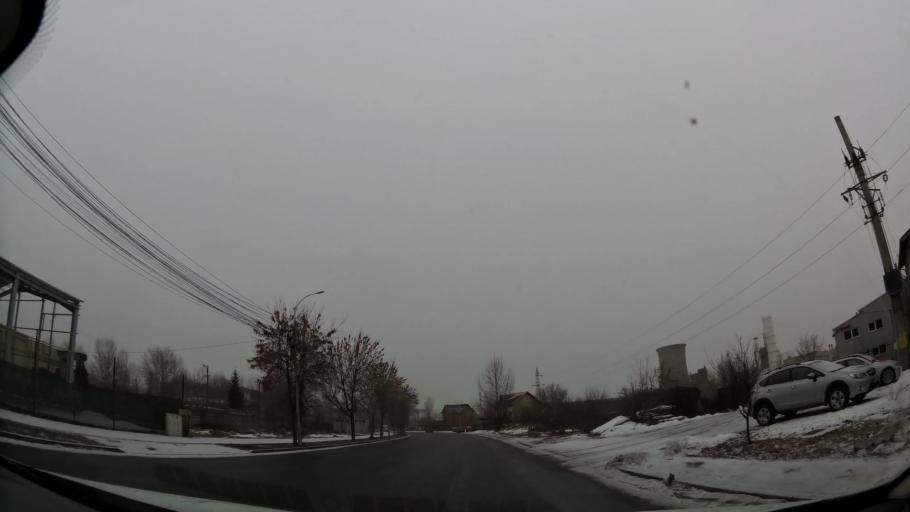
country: RO
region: Dambovita
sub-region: Municipiul Targoviste
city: Targoviste
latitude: 44.9133
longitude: 25.4439
